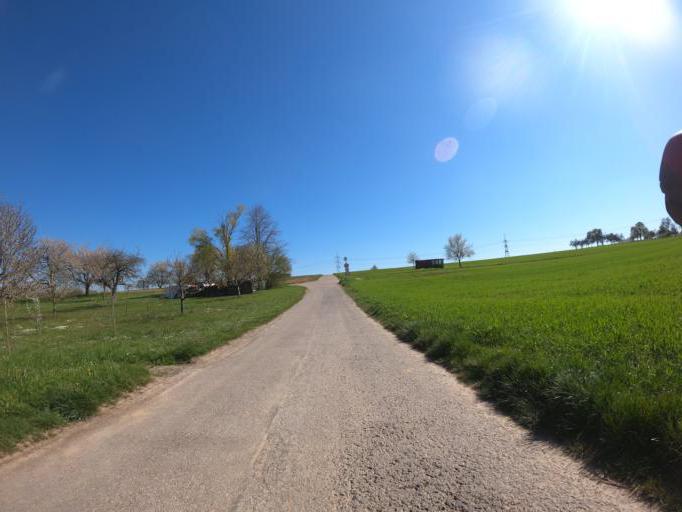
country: DE
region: Baden-Wuerttemberg
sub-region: Karlsruhe Region
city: Wiernsheim
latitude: 48.9061
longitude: 8.8538
